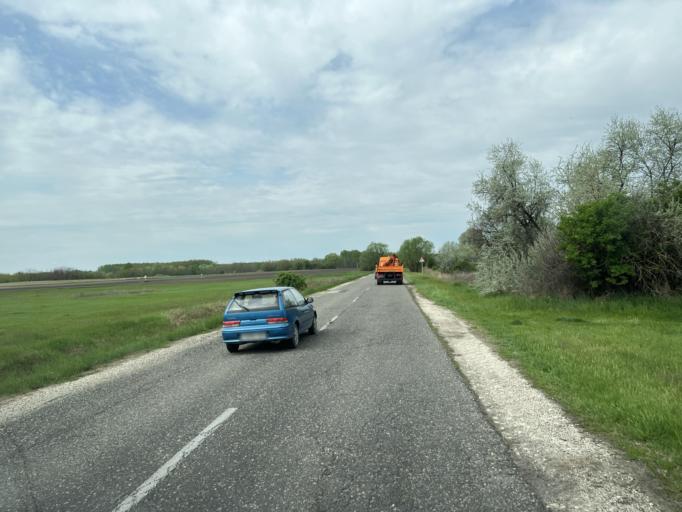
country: HU
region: Pest
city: Tortel
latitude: 47.1330
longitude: 19.9076
